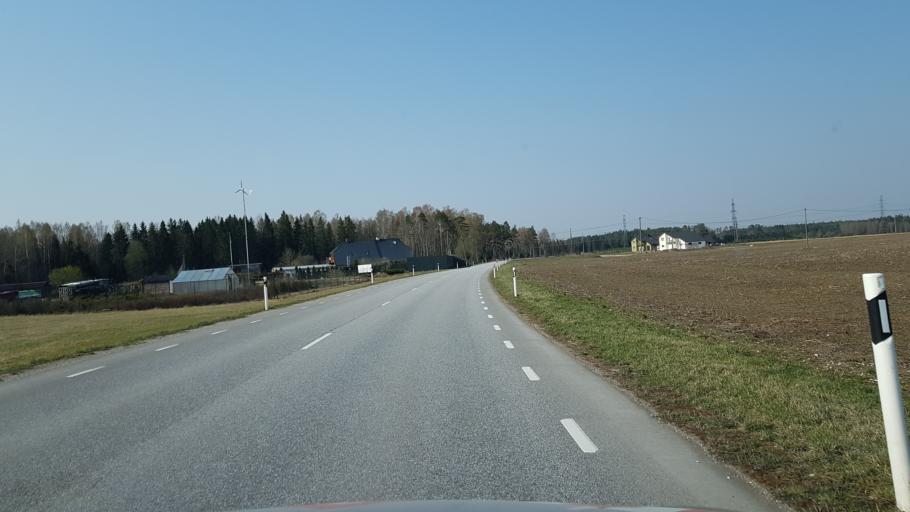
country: EE
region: Harju
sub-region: Saku vald
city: Saku
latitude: 59.2595
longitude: 24.7129
